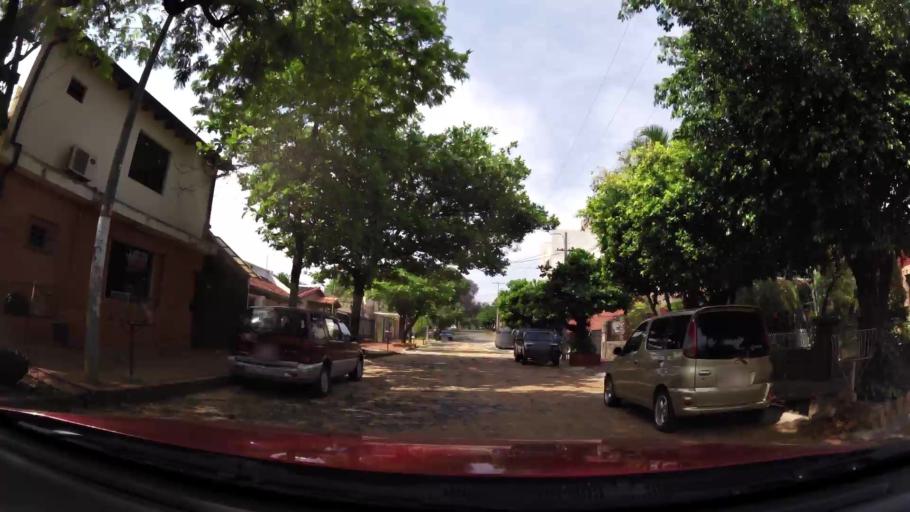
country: PY
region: Asuncion
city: Asuncion
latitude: -25.2643
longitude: -57.5646
